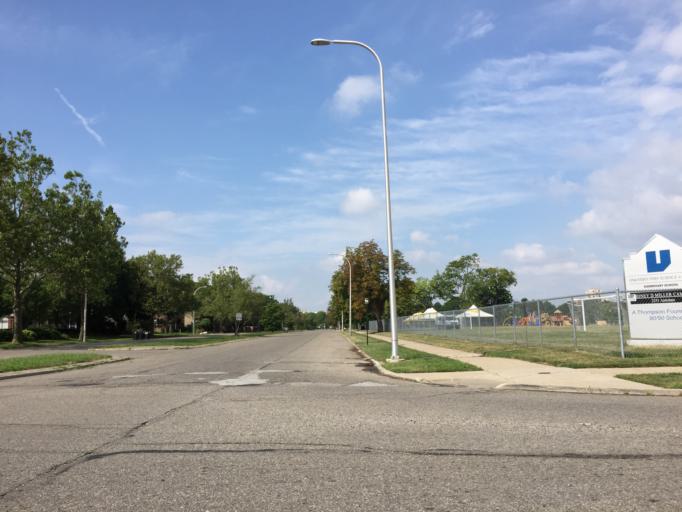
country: US
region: Michigan
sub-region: Wayne County
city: Detroit
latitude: 42.3478
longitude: -83.0292
